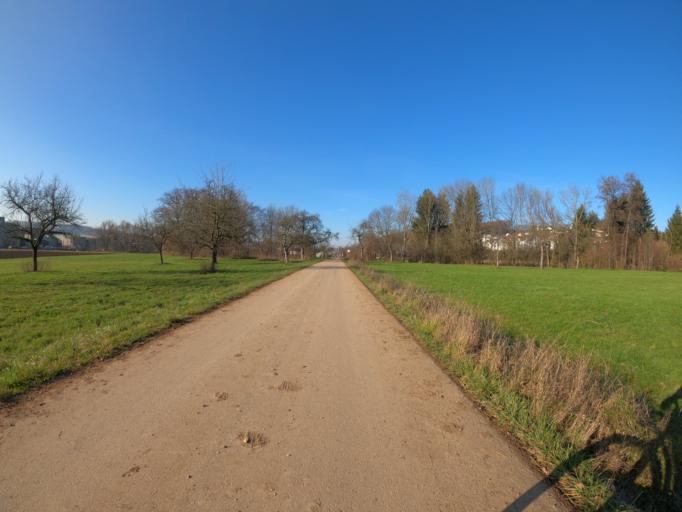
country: DE
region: Baden-Wuerttemberg
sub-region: Regierungsbezirk Stuttgart
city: Uhingen
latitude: 48.7086
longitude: 9.5974
